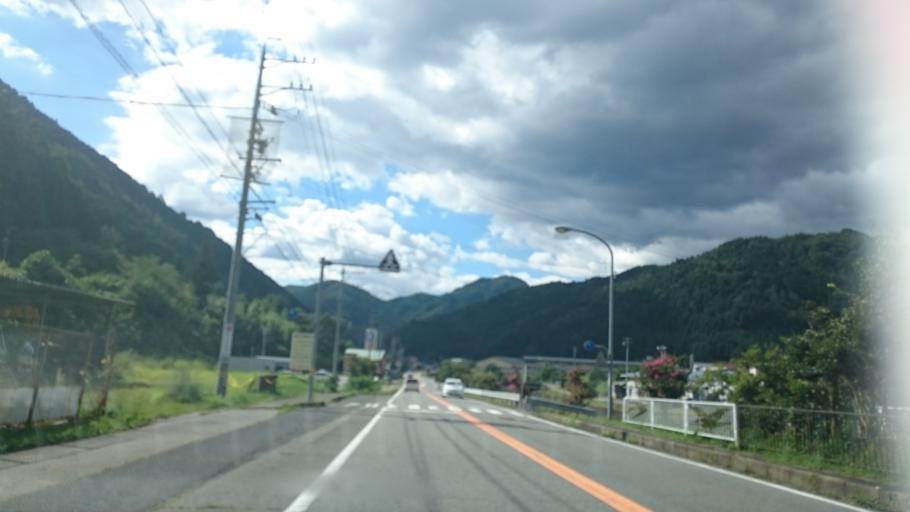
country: JP
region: Gifu
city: Gujo
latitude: 35.7648
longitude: 137.2888
